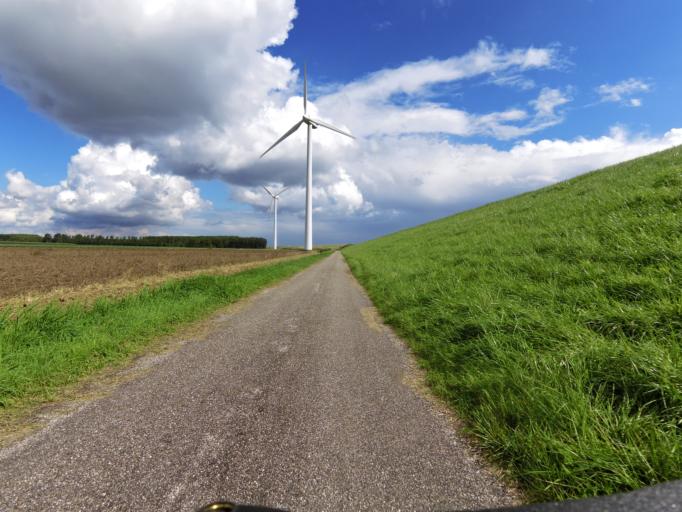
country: NL
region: North Brabant
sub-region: Gemeente Steenbergen
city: Dinteloord
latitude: 51.6695
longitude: 4.3514
